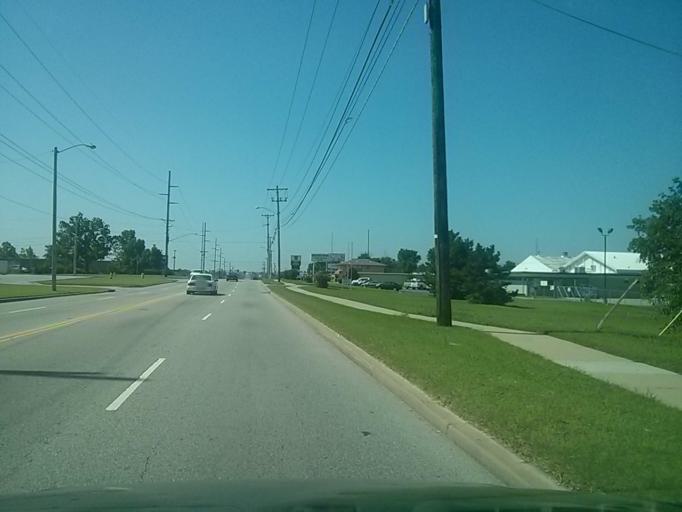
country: US
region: Oklahoma
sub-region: Tulsa County
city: Tulsa
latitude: 36.1436
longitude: -95.9047
